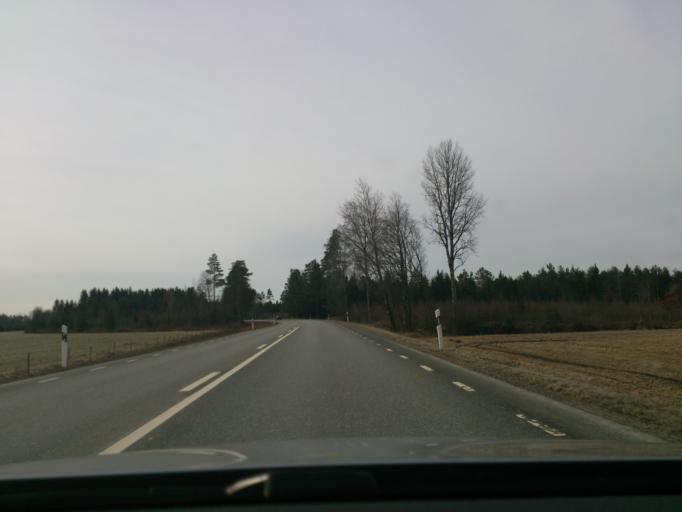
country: SE
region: Kronoberg
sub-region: Alvesta Kommun
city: Moheda
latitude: 56.9521
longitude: 14.5659
